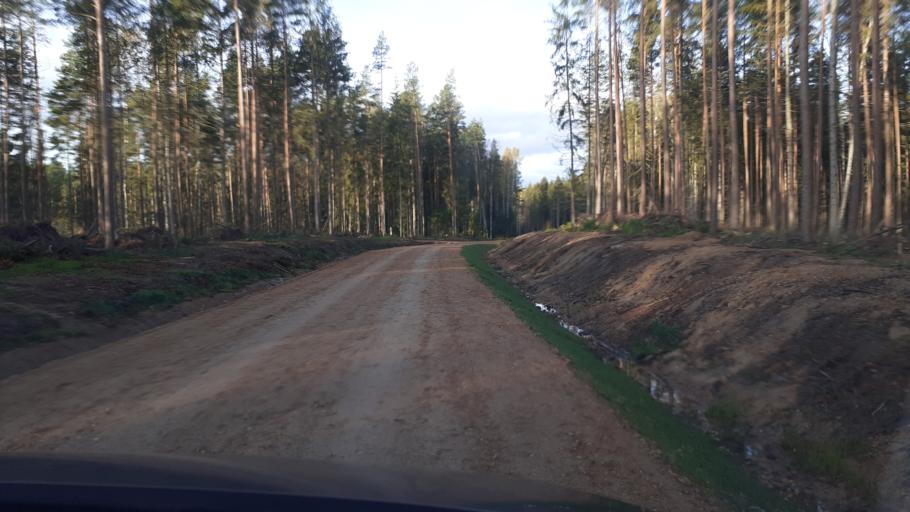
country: LV
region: Skrunda
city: Skrunda
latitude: 56.8488
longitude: 22.1011
